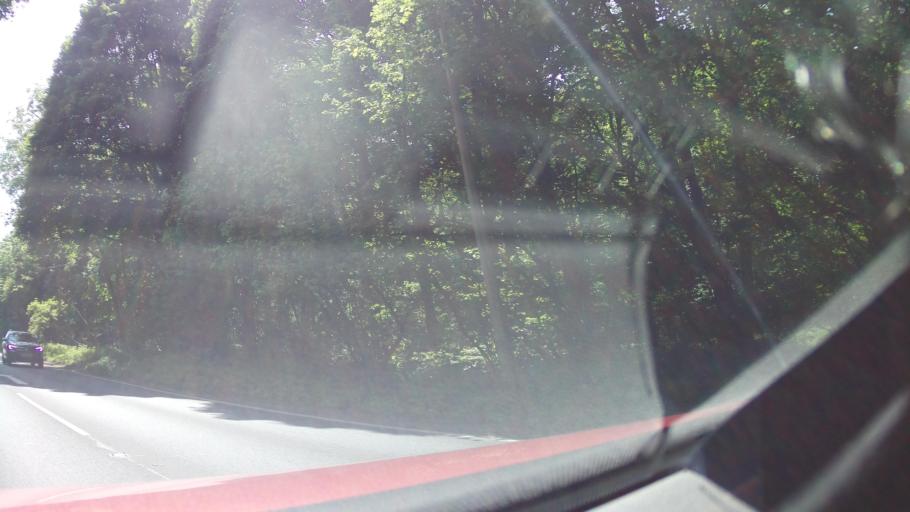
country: GB
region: England
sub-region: North Lincolnshire
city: Broughton
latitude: 53.5502
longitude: -0.5639
